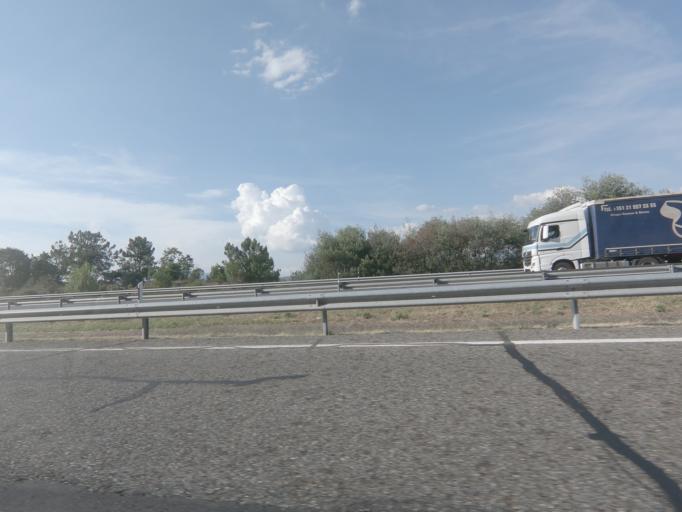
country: ES
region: Galicia
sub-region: Provincia de Ourense
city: Oimbra
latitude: 41.9245
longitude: -7.4840
